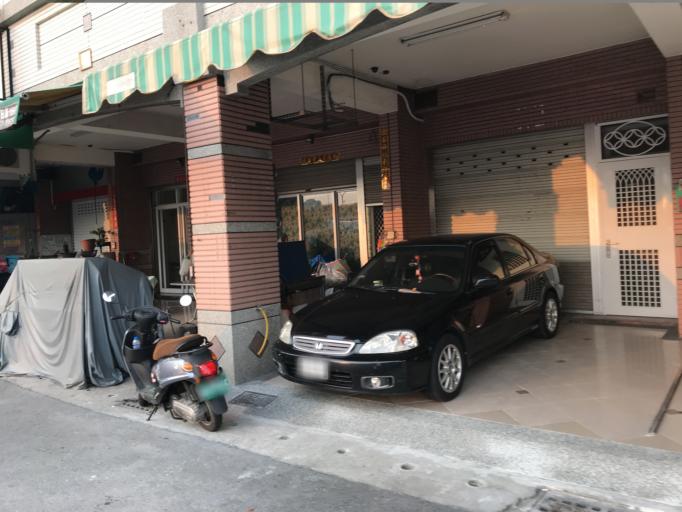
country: TW
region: Taiwan
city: Fengshan
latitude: 22.6772
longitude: 120.3312
